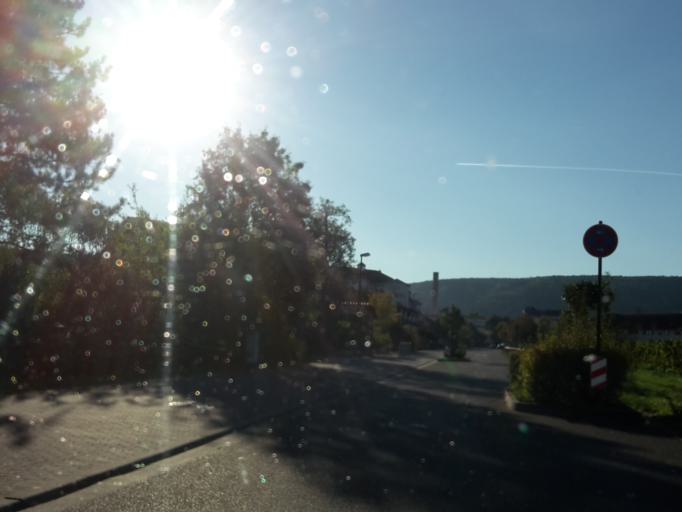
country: DE
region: Rheinland-Pfalz
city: Bad Duerkheim
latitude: 49.4684
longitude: 8.1854
